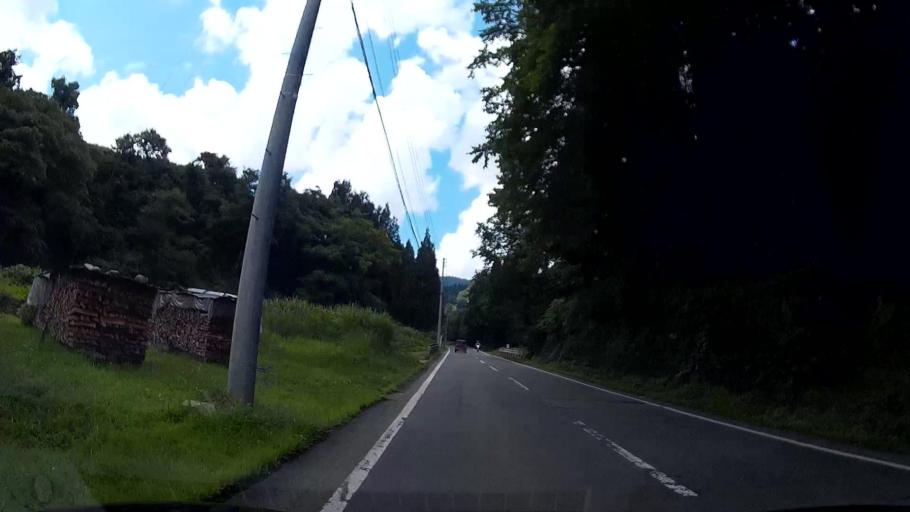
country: JP
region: Niigata
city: Shiozawa
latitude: 37.0198
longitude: 138.8168
